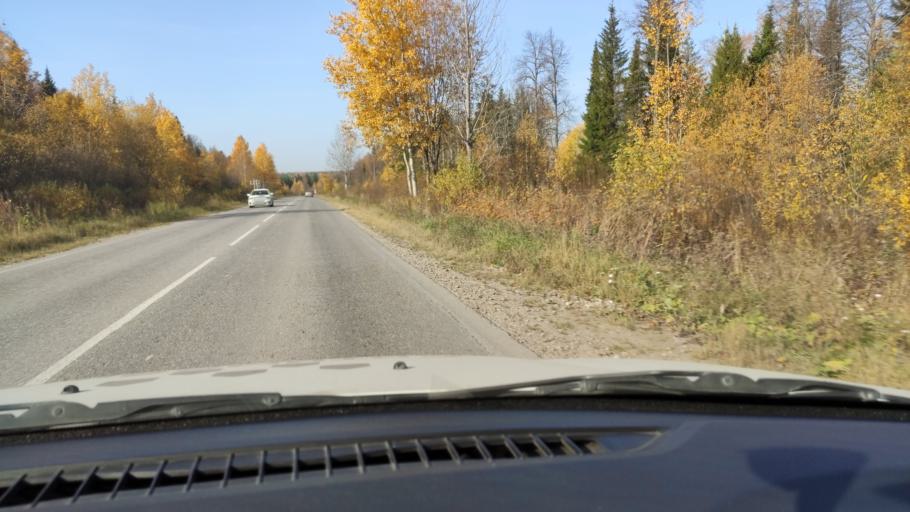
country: RU
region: Perm
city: Novyye Lyady
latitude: 58.0355
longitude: 56.6044
